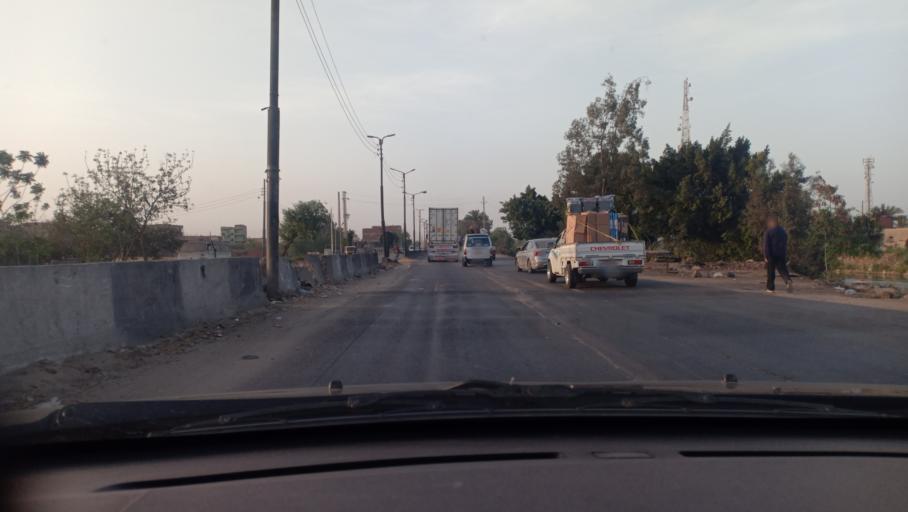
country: EG
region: Muhafazat al Gharbiyah
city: Zifta
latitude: 30.6228
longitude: 31.2786
